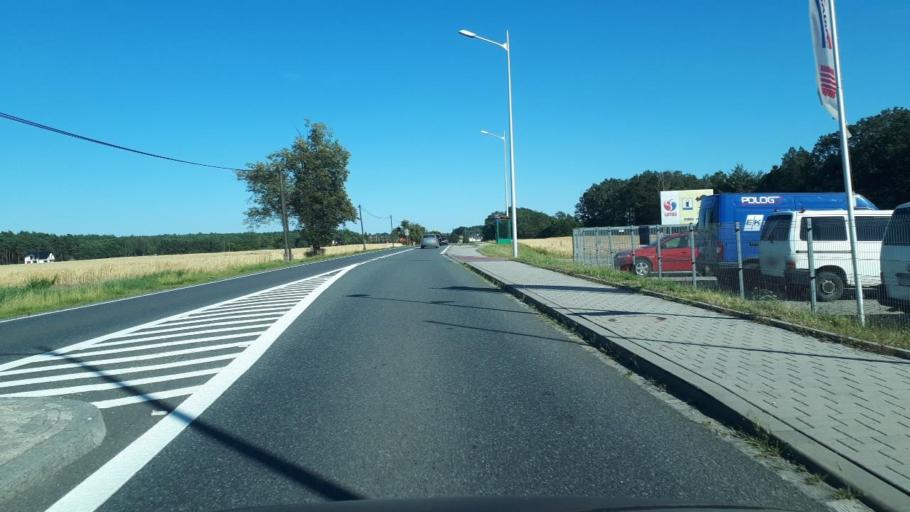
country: PL
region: Opole Voivodeship
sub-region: Powiat oleski
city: Olesno
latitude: 50.9022
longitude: 18.3810
